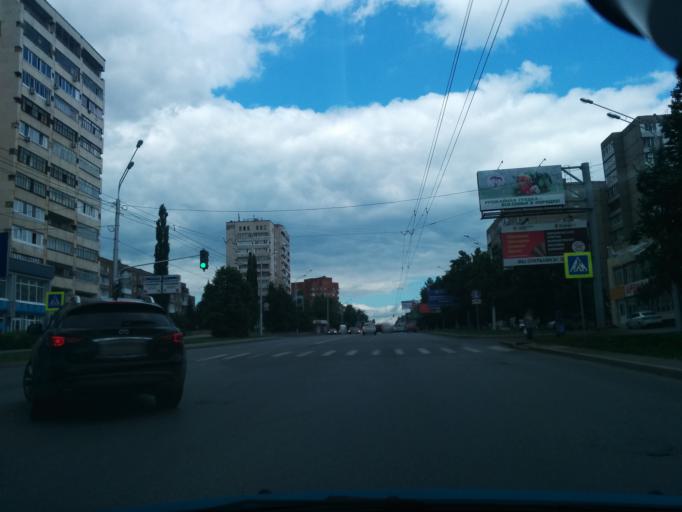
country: RU
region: Bashkortostan
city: Ufa
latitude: 54.7291
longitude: 55.9777
